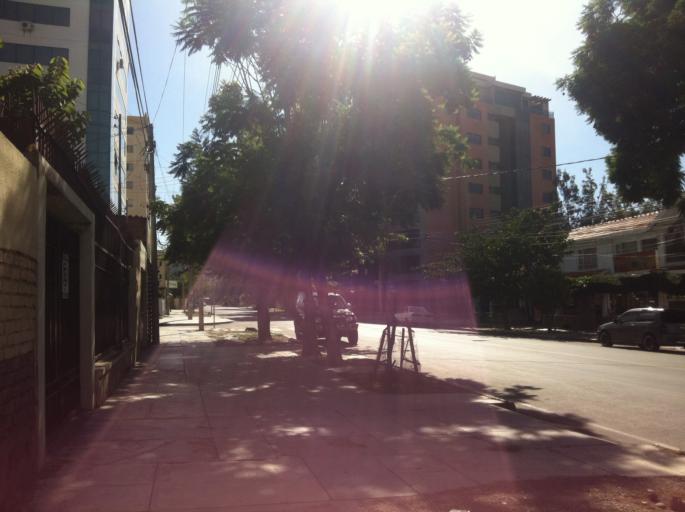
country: BO
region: Cochabamba
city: Cochabamba
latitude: -17.3808
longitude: -66.1503
